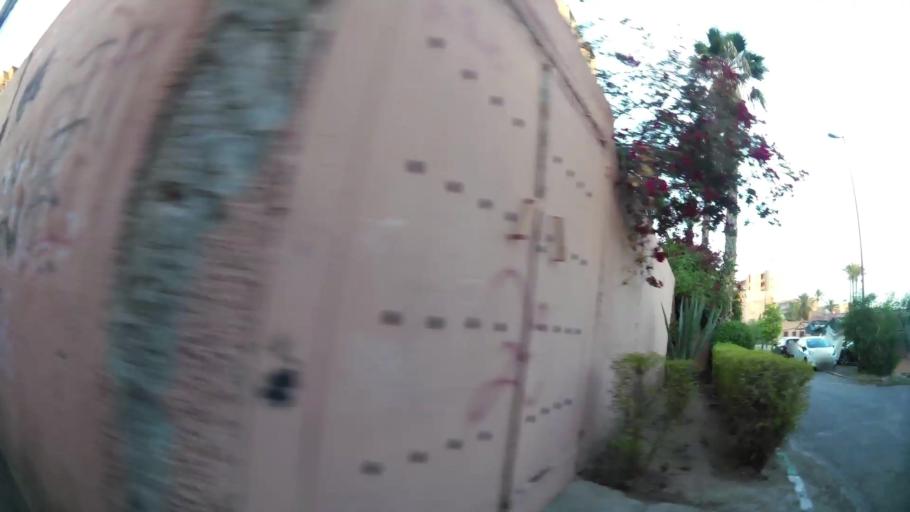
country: MA
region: Marrakech-Tensift-Al Haouz
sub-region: Marrakech
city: Marrakesh
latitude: 31.6385
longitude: -8.0243
